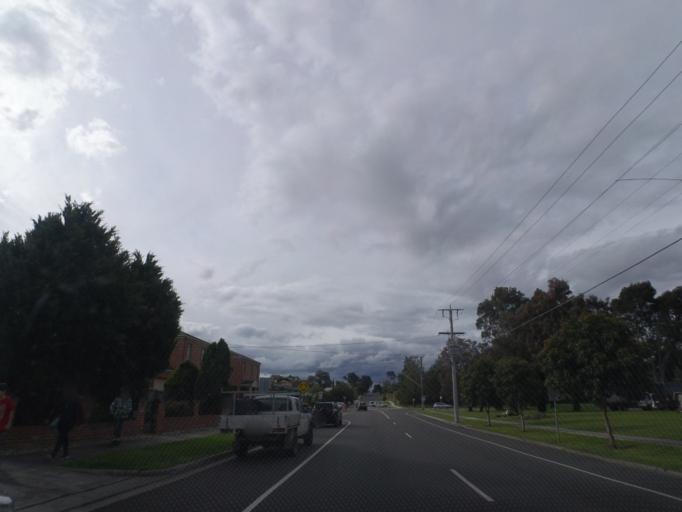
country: AU
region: Victoria
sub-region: Yarra Ranges
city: Lilydale
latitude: -37.7514
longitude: 145.3440
